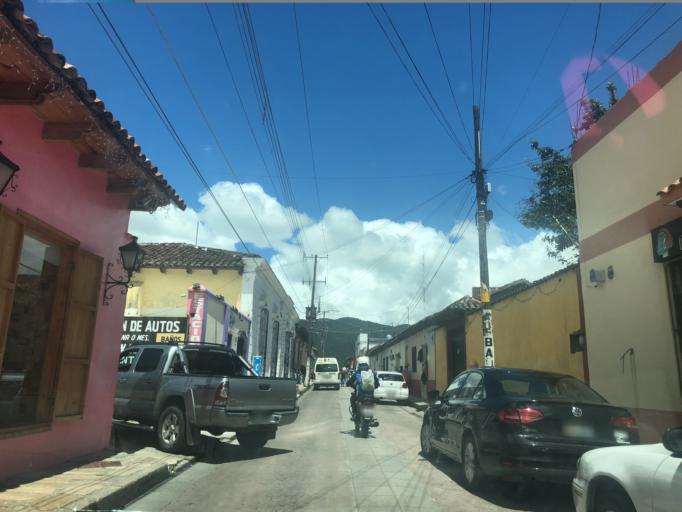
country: MX
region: Chiapas
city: San Cristobal de las Casas
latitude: 16.7333
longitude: -92.6390
